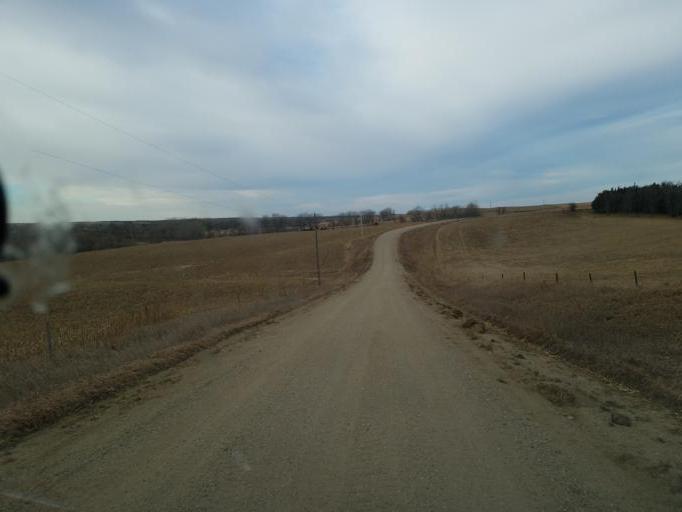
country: US
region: Nebraska
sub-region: Knox County
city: Bloomfield
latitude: 42.5576
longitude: -97.7472
